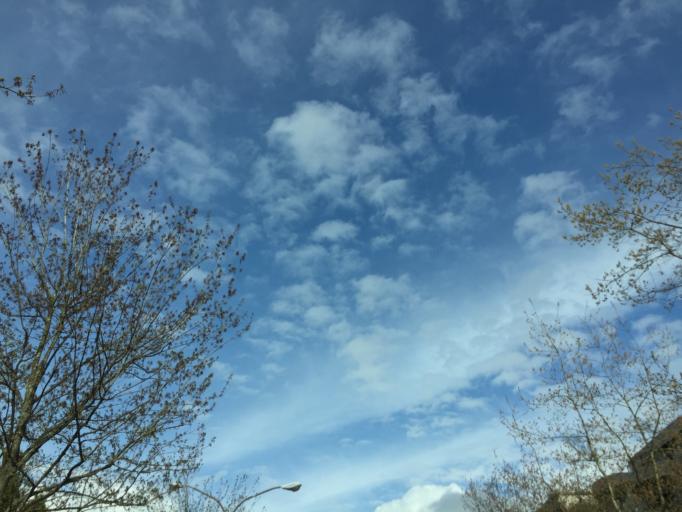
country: CA
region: British Columbia
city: Richmond
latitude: 49.1627
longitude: -123.1302
